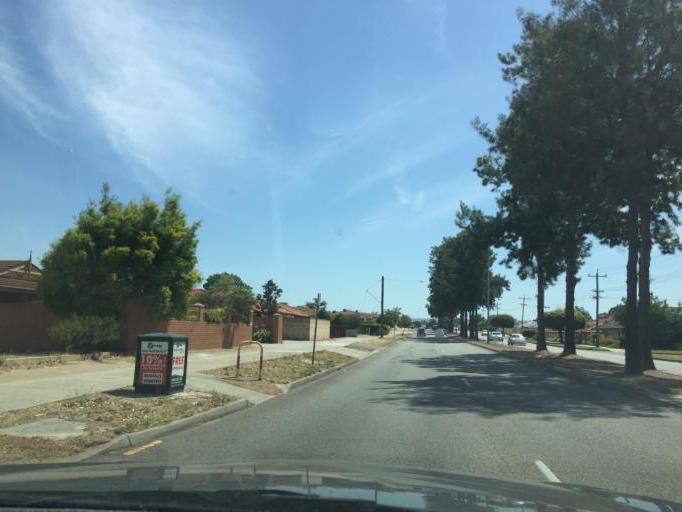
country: AU
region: Western Australia
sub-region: Gosnells
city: Thornlie
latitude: -32.0739
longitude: 115.9628
